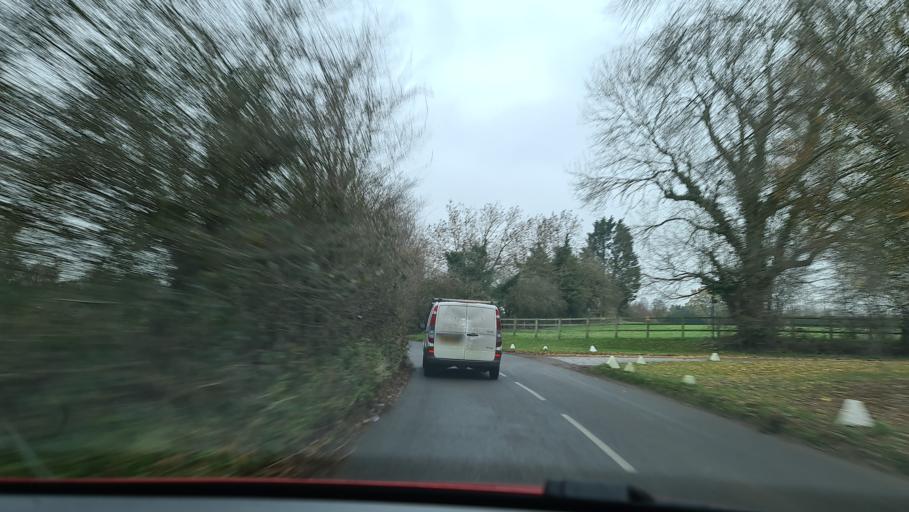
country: GB
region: England
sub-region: Buckinghamshire
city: Seer Green
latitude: 51.6204
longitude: -0.5900
